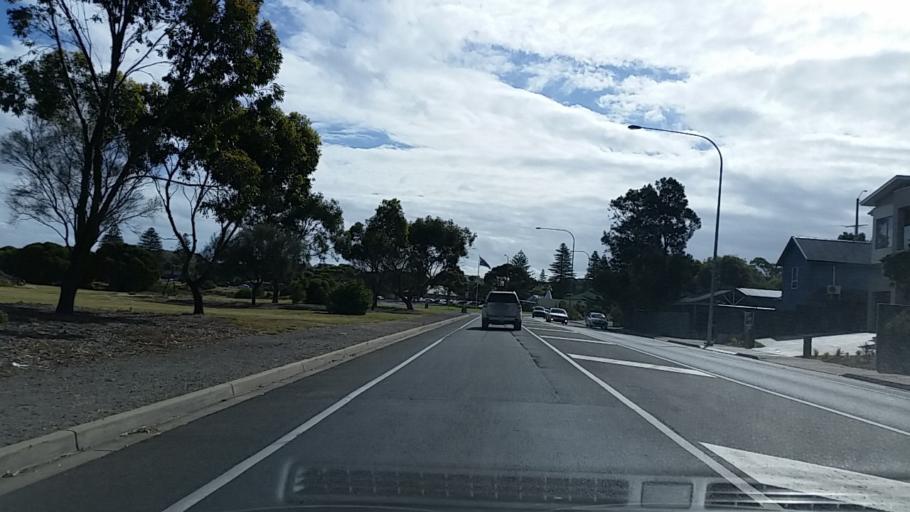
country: AU
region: South Australia
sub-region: Adelaide
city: Port Noarlunga
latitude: -35.1484
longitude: 138.4746
